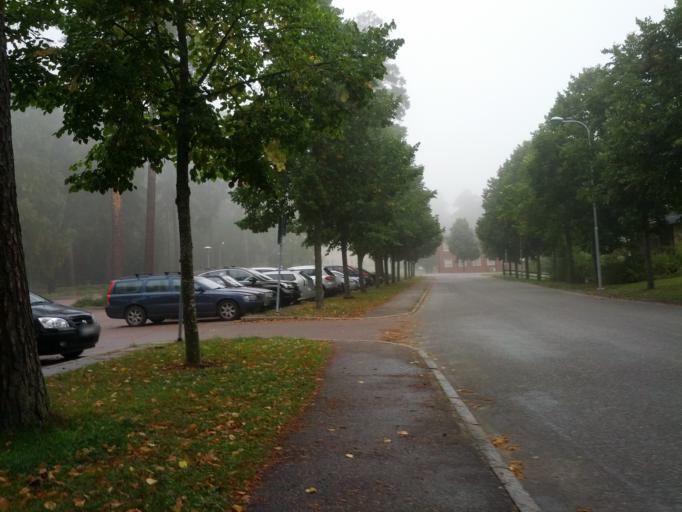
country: SE
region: Uppsala
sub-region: Uppsala Kommun
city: Uppsala
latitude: 59.8319
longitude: 17.6471
